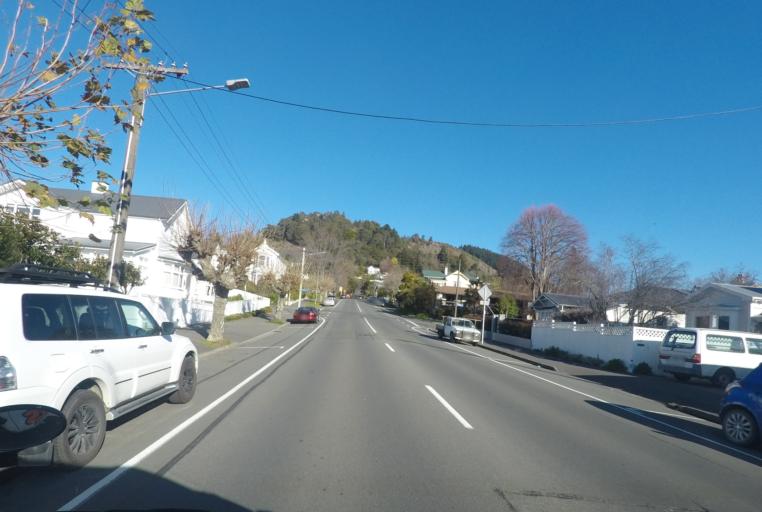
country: NZ
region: Nelson
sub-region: Nelson City
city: Nelson
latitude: -41.2794
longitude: 173.2867
